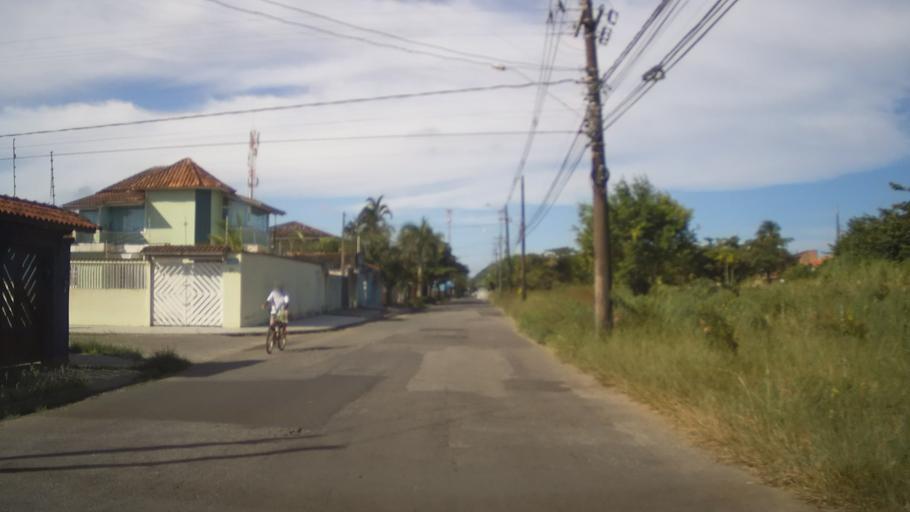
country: BR
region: Sao Paulo
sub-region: Itanhaem
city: Itanhaem
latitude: -24.1988
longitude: -46.8205
